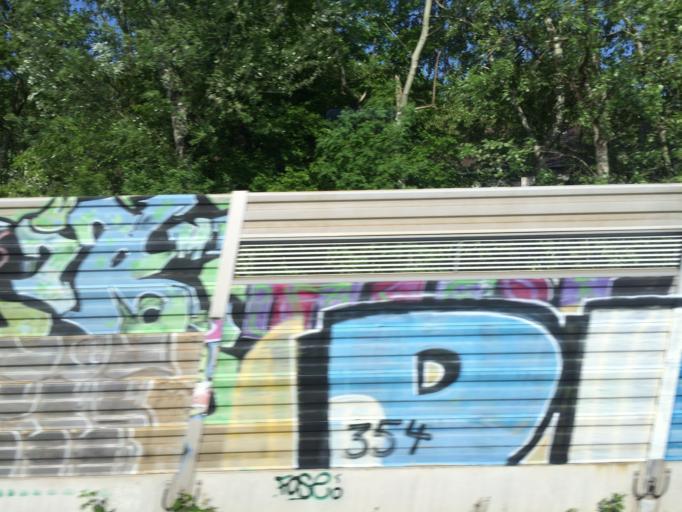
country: DE
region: North Rhine-Westphalia
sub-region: Regierungsbezirk Koln
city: Porz am Rhein
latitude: 50.8851
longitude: 7.0634
